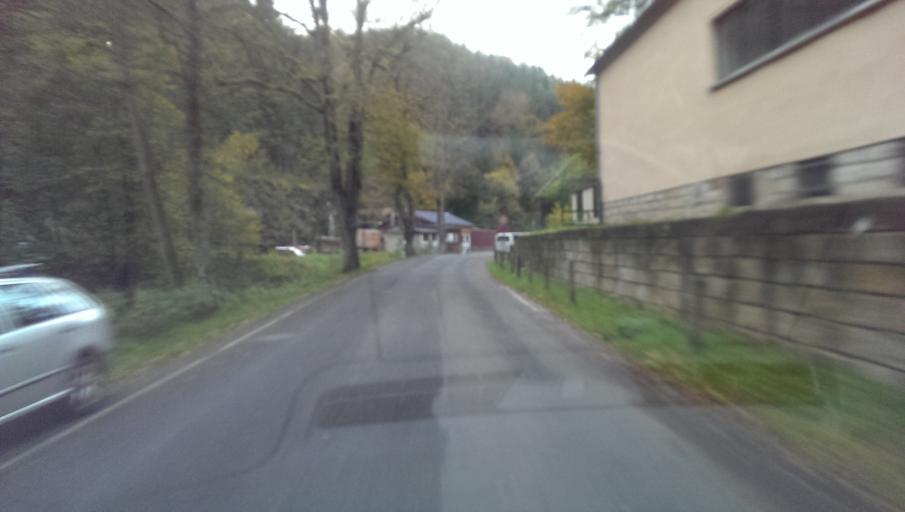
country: DE
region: Saxony
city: Sebnitz
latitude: 50.9252
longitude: 14.2774
